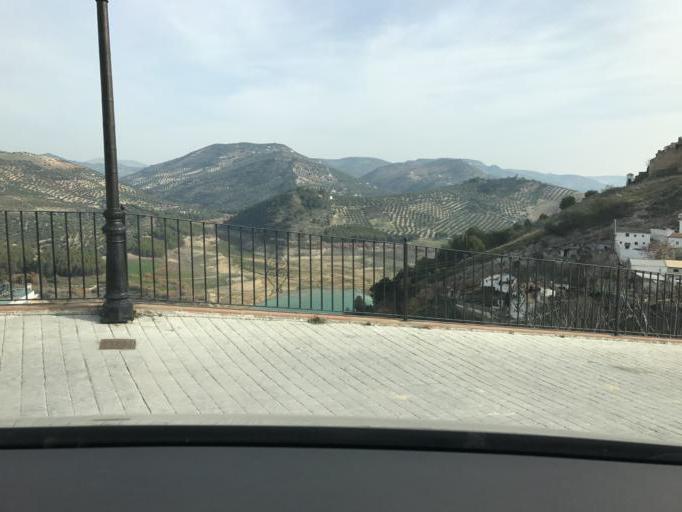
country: ES
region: Andalusia
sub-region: Province of Cordoba
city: Iznajar
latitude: 37.2583
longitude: -4.3112
